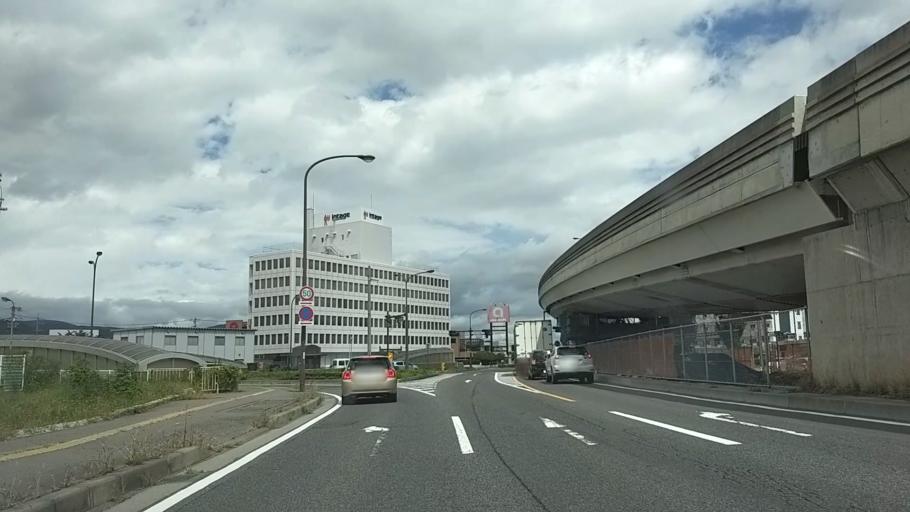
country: JP
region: Nagano
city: Nagano-shi
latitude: 36.6280
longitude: 138.2011
